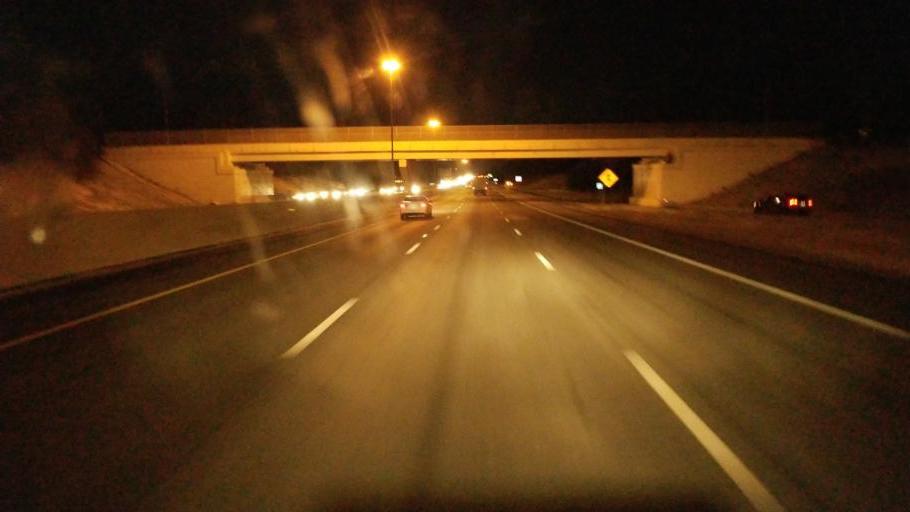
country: US
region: Ohio
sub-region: Montgomery County
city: Vandalia
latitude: 39.8646
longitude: -84.2258
